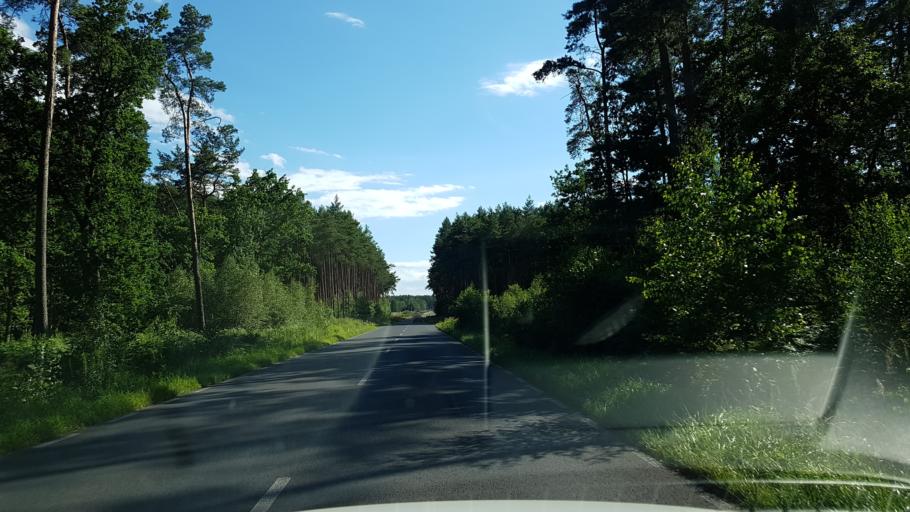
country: PL
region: West Pomeranian Voivodeship
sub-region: Powiat goleniowski
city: Goleniow
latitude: 53.5715
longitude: 14.7888
